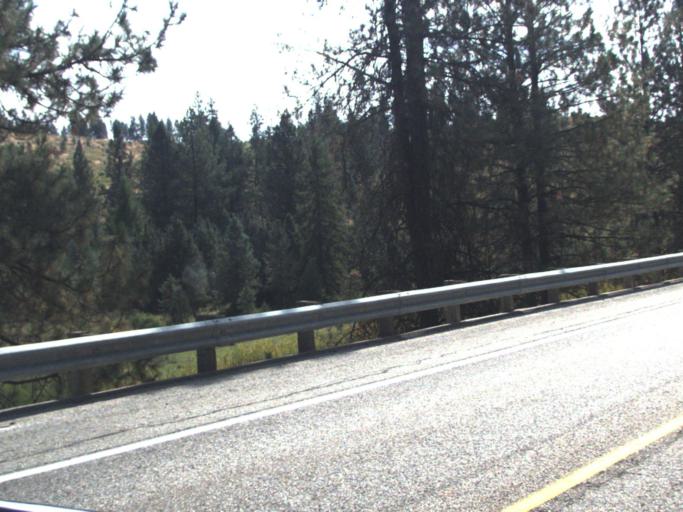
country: US
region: Washington
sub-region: Stevens County
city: Chewelah
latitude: 48.1775
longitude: -117.7015
